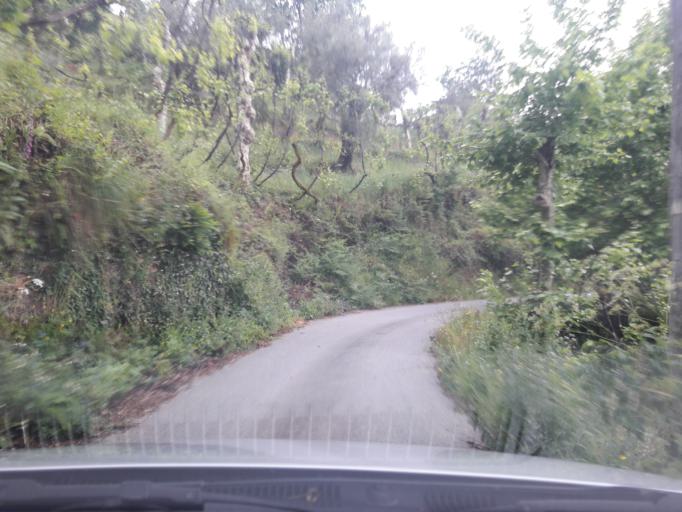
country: PT
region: Braga
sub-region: Celorico de Basto
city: Celorico de Basto
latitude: 41.3838
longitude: -8.0440
